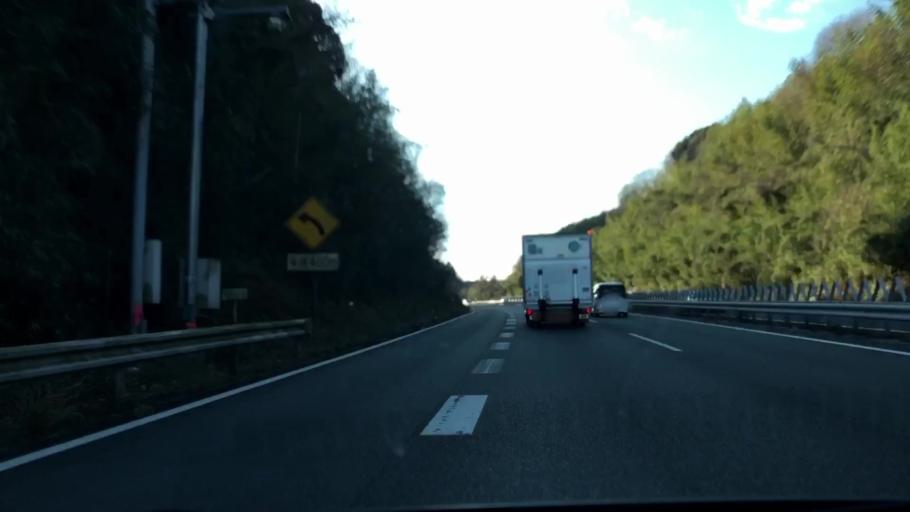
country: JP
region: Yamaguchi
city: Onoda
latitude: 34.1172
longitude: 131.1143
